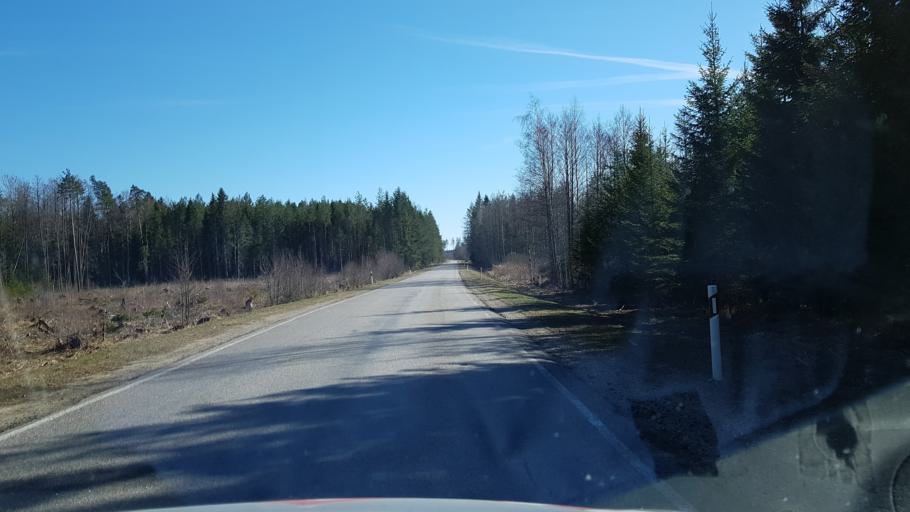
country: EE
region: Laeaene-Virumaa
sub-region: Vinni vald
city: Vinni
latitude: 59.2544
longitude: 26.6872
